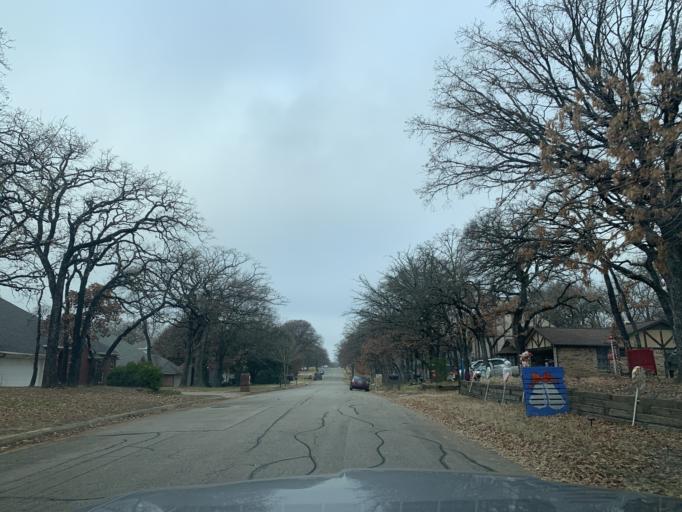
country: US
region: Texas
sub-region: Tarrant County
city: Bedford
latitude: 32.8336
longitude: -97.1448
